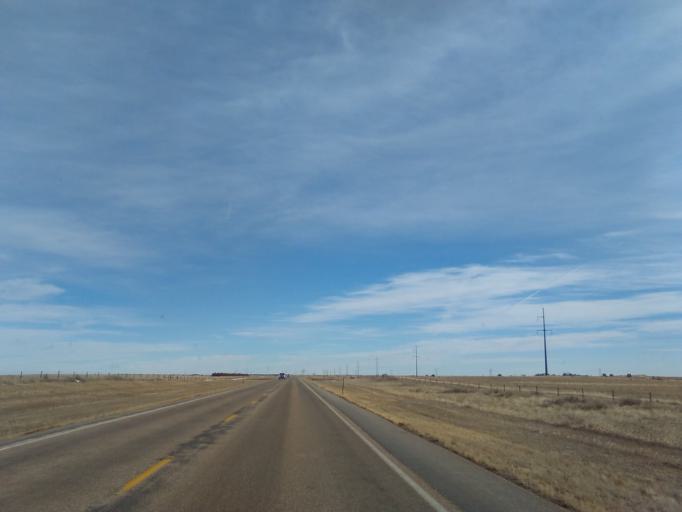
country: US
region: Wyoming
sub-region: Laramie County
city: Pine Bluffs
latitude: 41.4269
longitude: -104.3861
